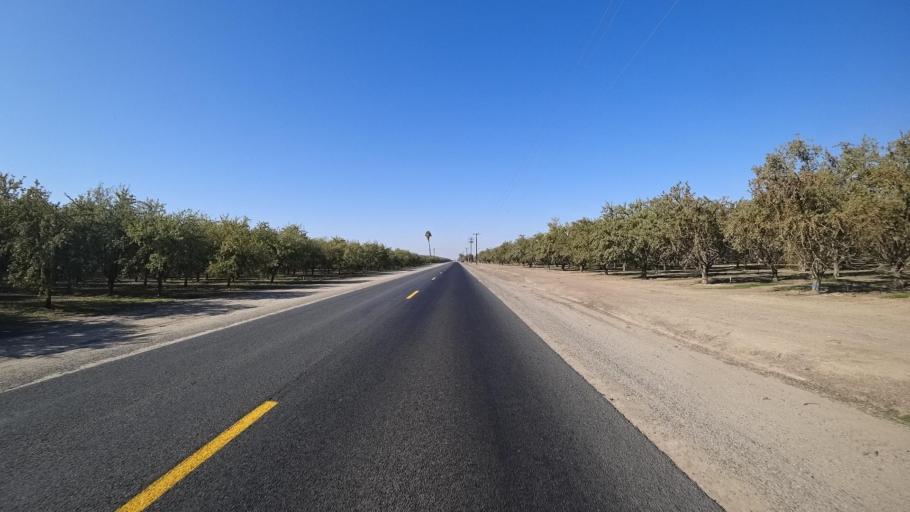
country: US
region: California
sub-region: Kern County
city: Wasco
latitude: 35.7176
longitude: -119.3722
